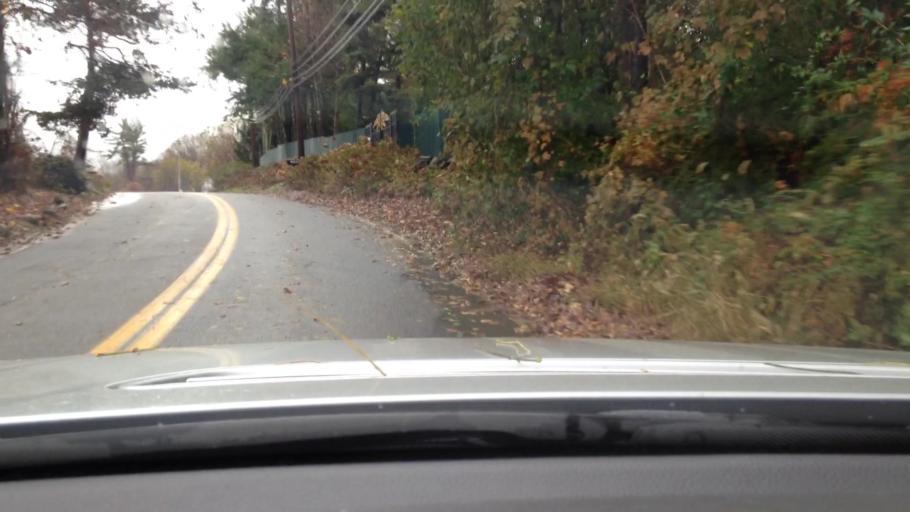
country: US
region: New York
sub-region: Westchester County
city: Croton-on-Hudson
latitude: 41.2257
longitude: -73.8767
